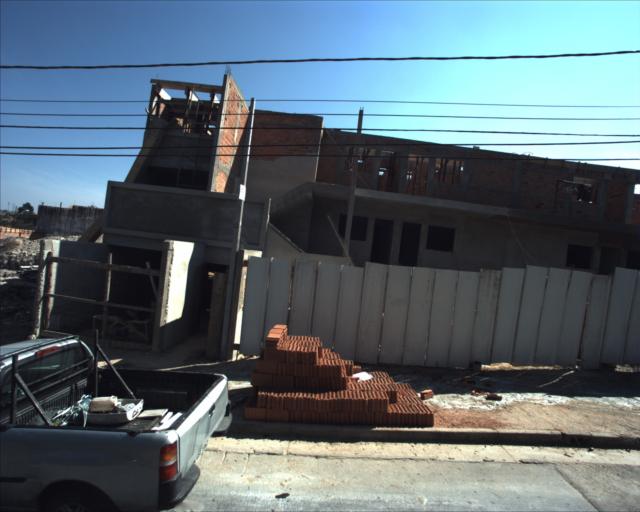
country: BR
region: Sao Paulo
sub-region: Sorocaba
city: Sorocaba
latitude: -23.4727
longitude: -47.4343
